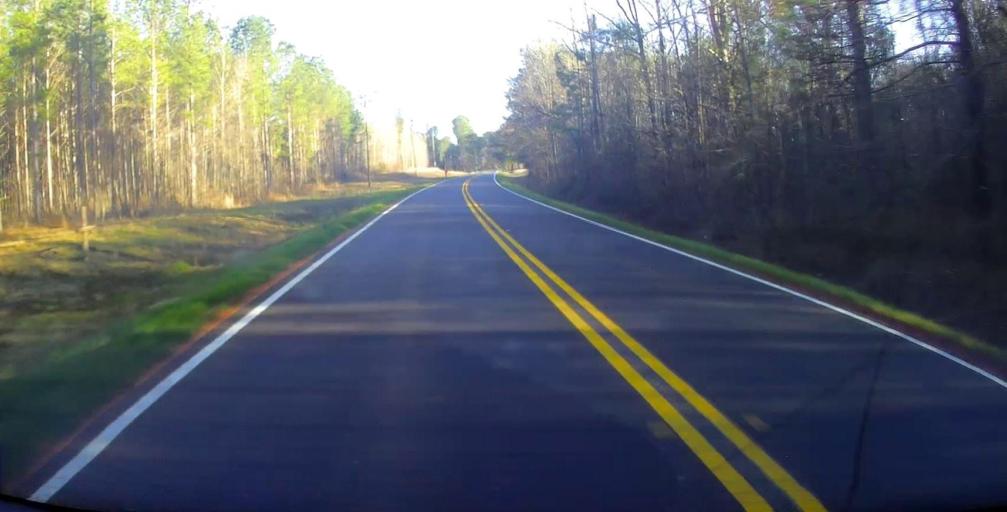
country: US
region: Georgia
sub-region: Meriwether County
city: Manchester
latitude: 32.8990
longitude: -84.7162
